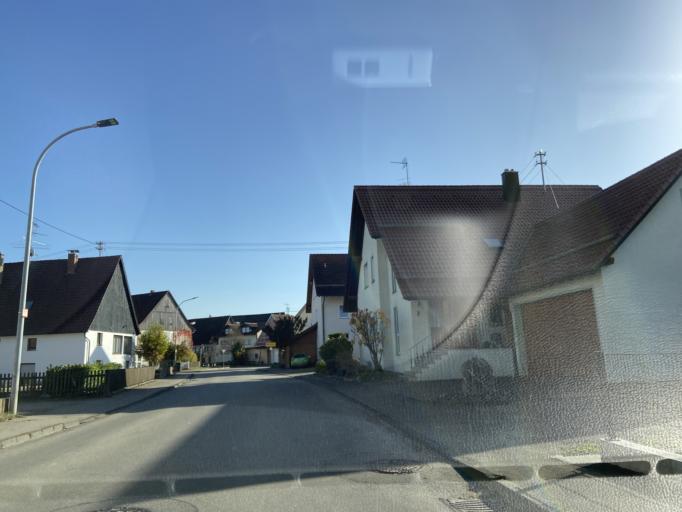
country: DE
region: Baden-Wuerttemberg
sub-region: Tuebingen Region
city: Ennetach
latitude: 48.0292
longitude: 9.2938
